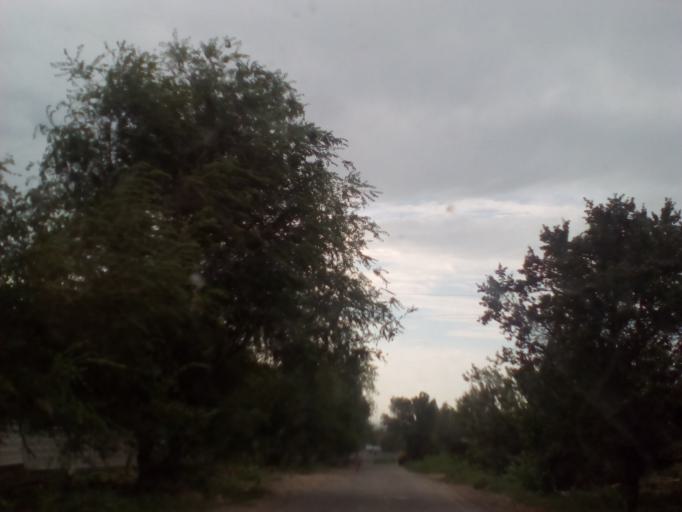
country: KZ
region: Almaty Oblysy
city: Burunday
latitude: 43.1584
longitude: 76.3835
